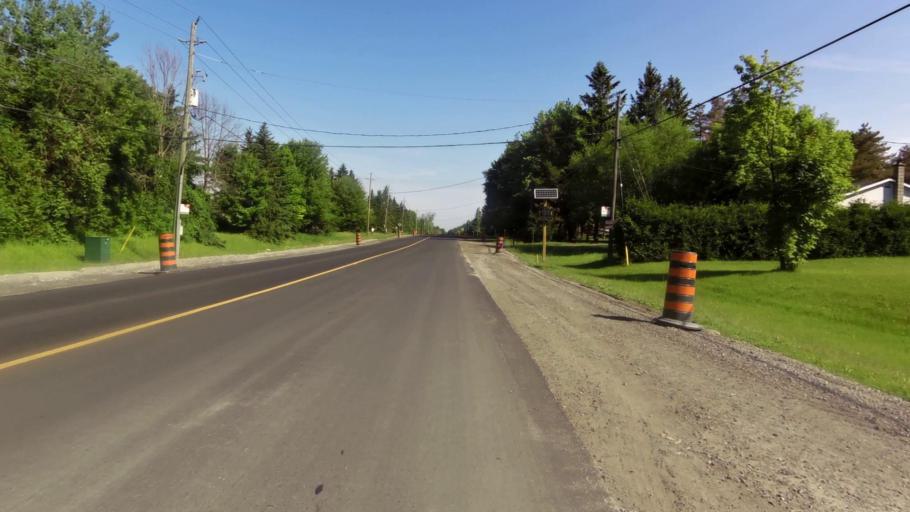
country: CA
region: Ontario
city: Ottawa
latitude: 45.2502
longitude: -75.5901
